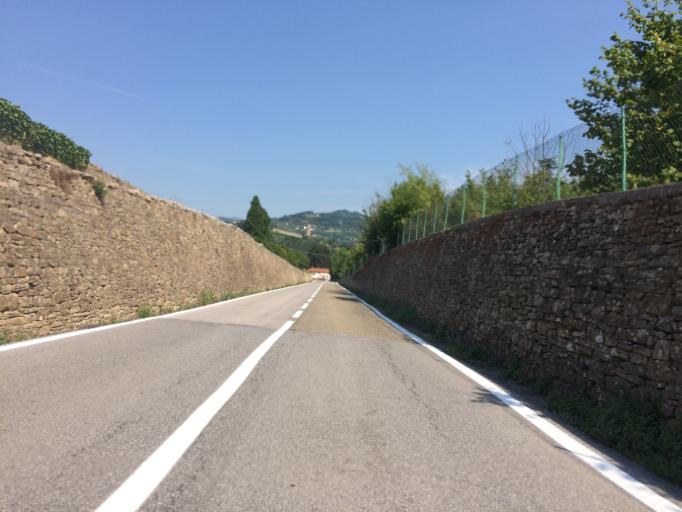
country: IT
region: Piedmont
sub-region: Provincia di Cuneo
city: Cortemilia
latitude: 44.5826
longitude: 8.1754
